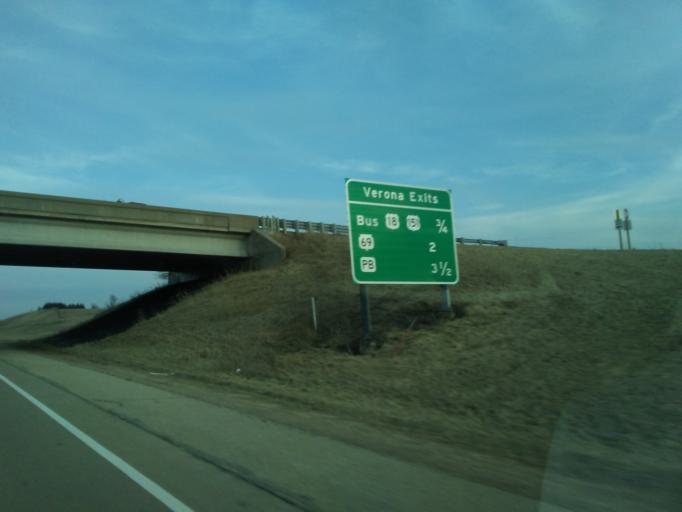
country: US
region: Wisconsin
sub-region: Dane County
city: Verona
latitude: 42.9873
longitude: -89.5832
